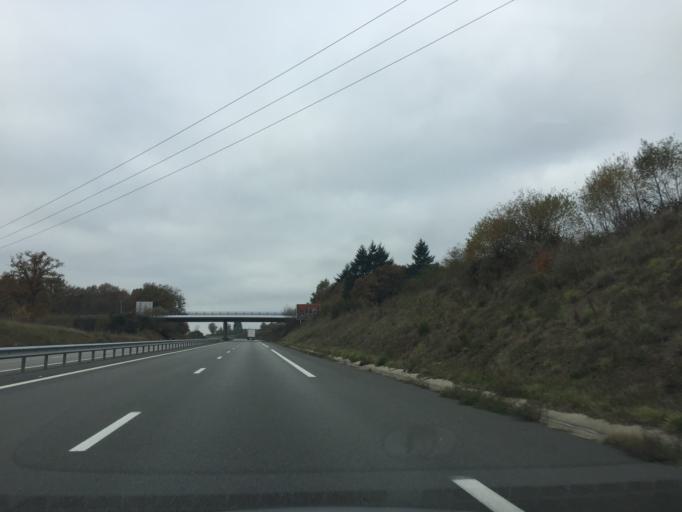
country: FR
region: Limousin
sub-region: Departement de la Creuse
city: Gouzon
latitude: 46.2390
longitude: 2.3283
